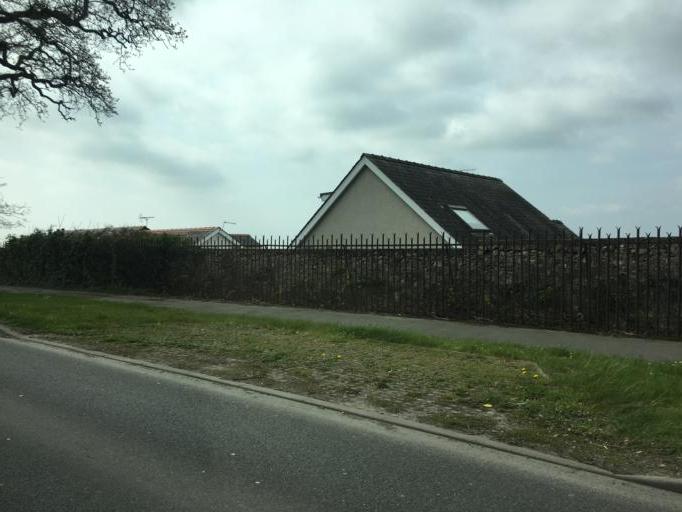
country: GB
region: Wales
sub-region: Gwynedd
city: Caernarfon
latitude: 53.1494
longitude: -4.2654
